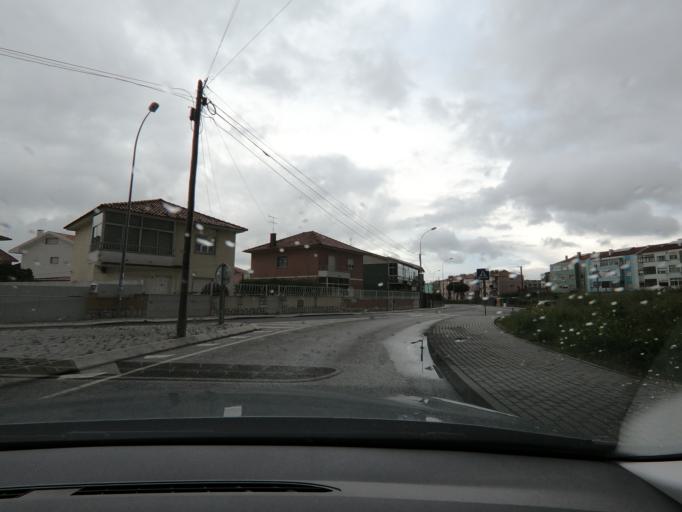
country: PT
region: Lisbon
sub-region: Sintra
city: Sintra
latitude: 38.7990
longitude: -9.3508
